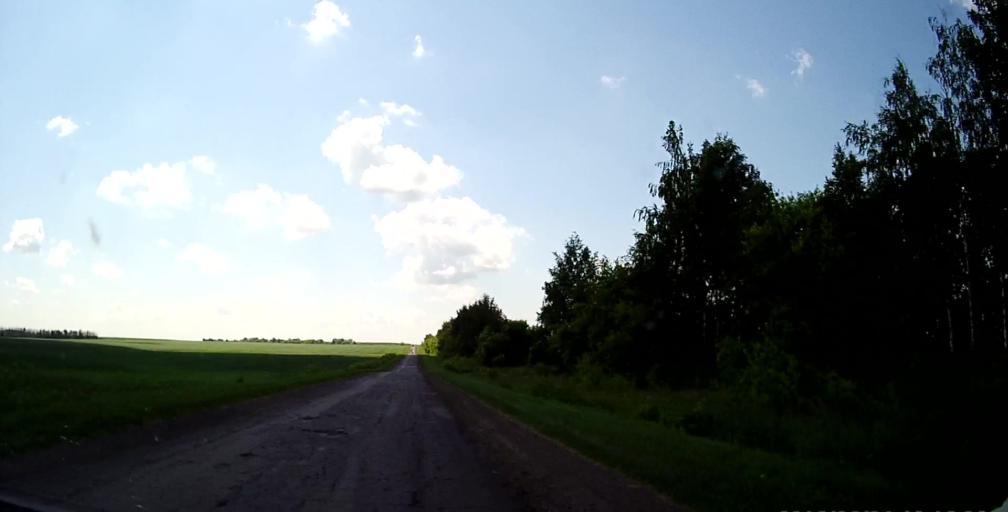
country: RU
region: Lipetsk
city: Chaplygin
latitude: 53.2848
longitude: 39.9600
